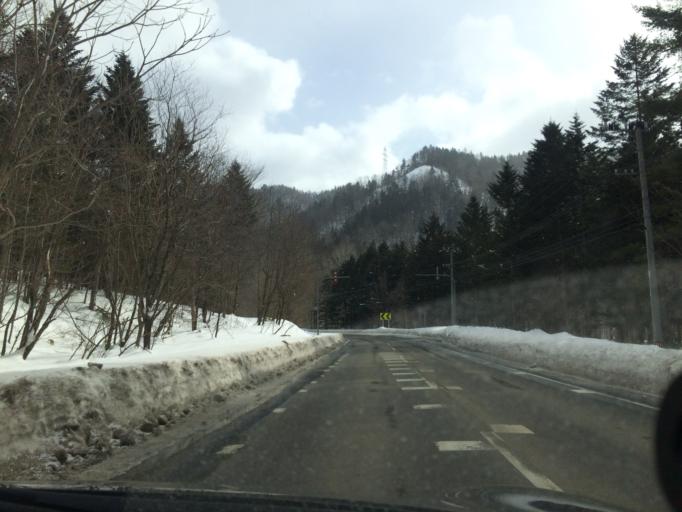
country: JP
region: Hokkaido
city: Shimo-furano
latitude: 43.0515
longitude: 142.4971
